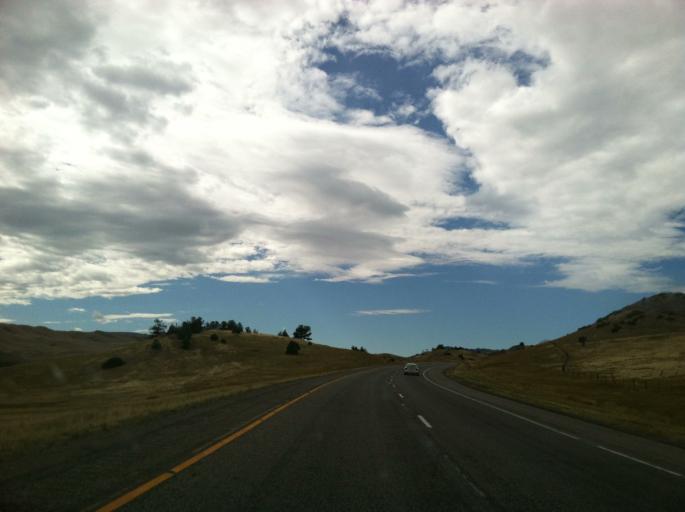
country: US
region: Montana
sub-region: Park County
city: Livingston
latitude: 45.6611
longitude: -110.6536
